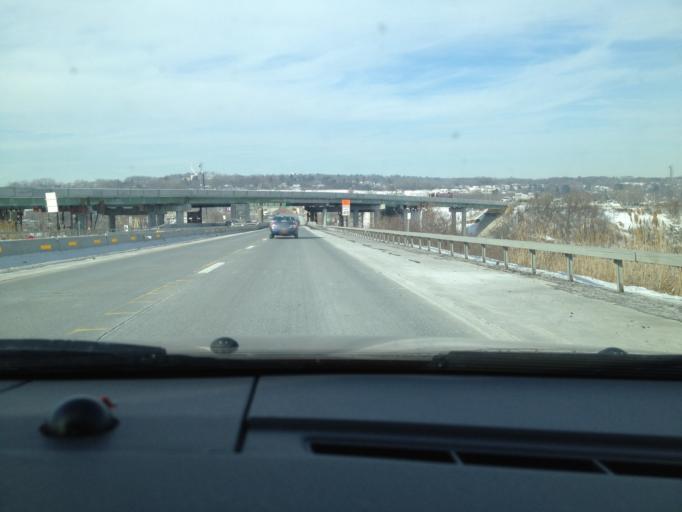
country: US
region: New York
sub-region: Rensselaer County
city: Rensselaer
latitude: 42.6664
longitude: -73.7314
